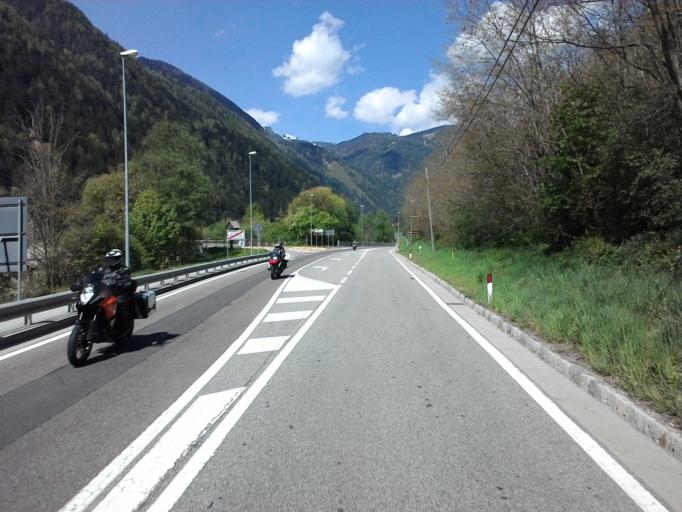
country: IT
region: Trentino-Alto Adige
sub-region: Bolzano
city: Fortezza
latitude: 46.8082
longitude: 11.5730
